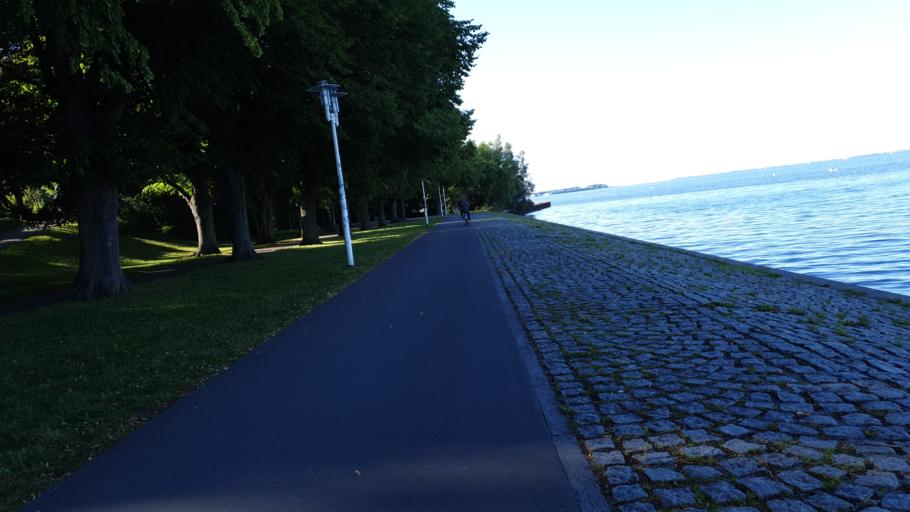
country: DE
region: Mecklenburg-Vorpommern
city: Stralsund
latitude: 54.3251
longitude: 13.0866
